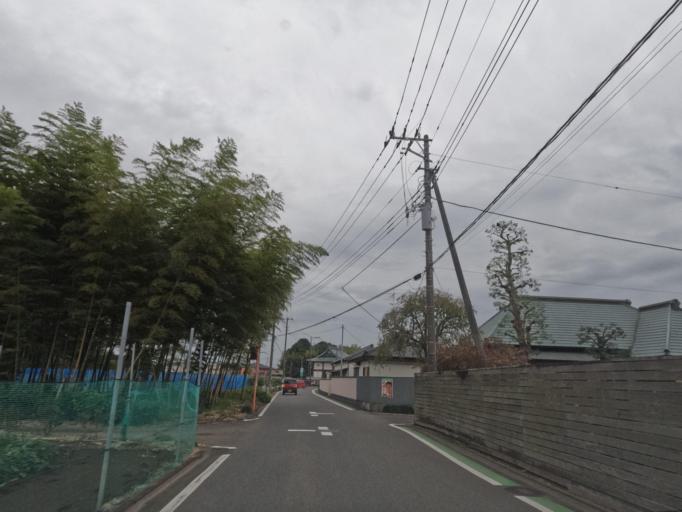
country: JP
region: Saitama
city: Saitama
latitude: 35.8900
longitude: 139.7060
